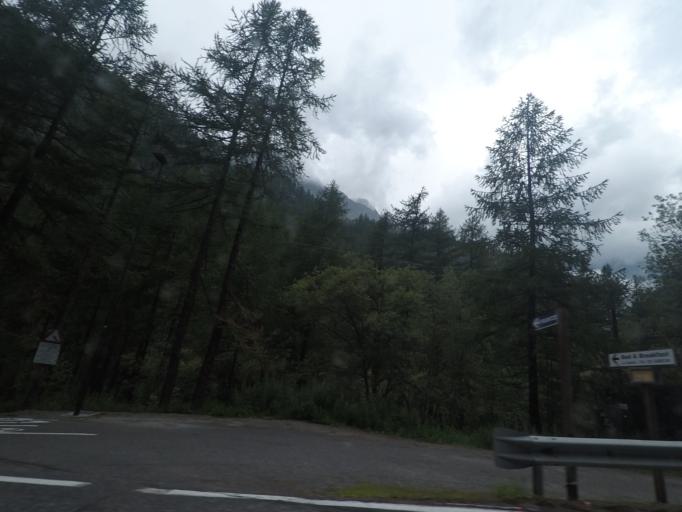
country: IT
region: Aosta Valley
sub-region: Valle d'Aosta
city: Paquier
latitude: 45.9011
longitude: 7.6170
